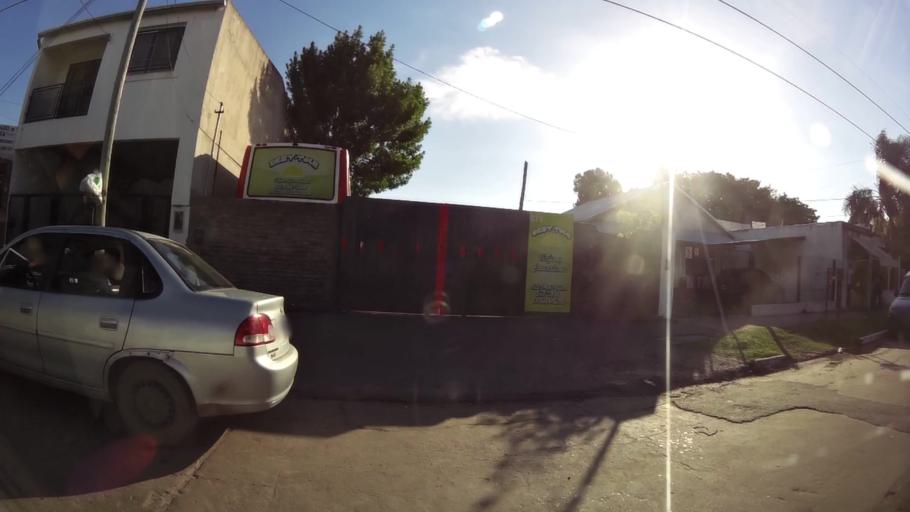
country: AR
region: Buenos Aires
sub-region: Partido de Merlo
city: Merlo
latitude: -34.6865
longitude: -58.7324
